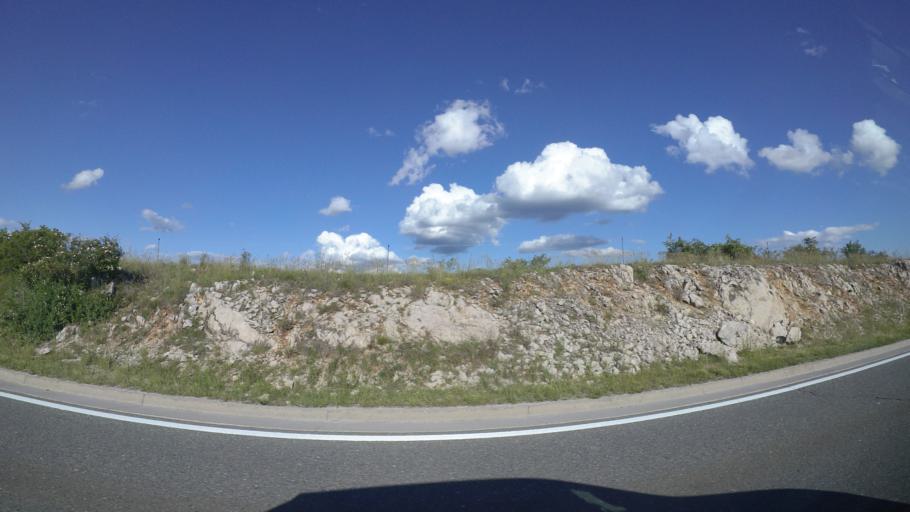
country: HR
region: Zadarska
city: Gracac
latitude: 44.5175
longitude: 15.7443
